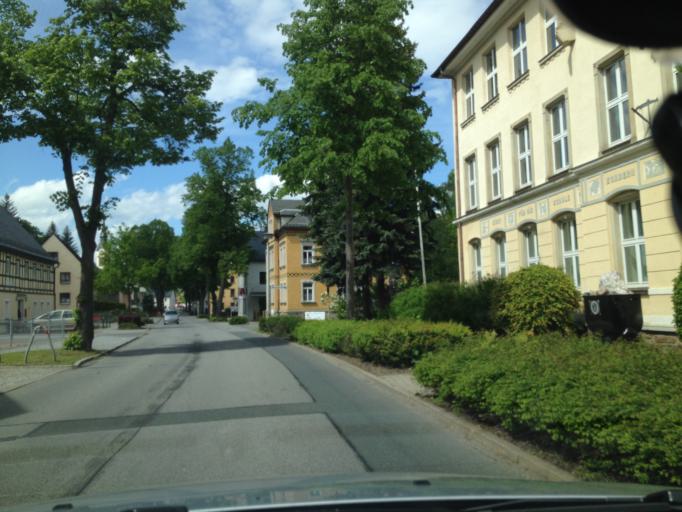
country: DE
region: Saxony
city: Annaberg-Buchholz
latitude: 50.5353
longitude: 12.9953
